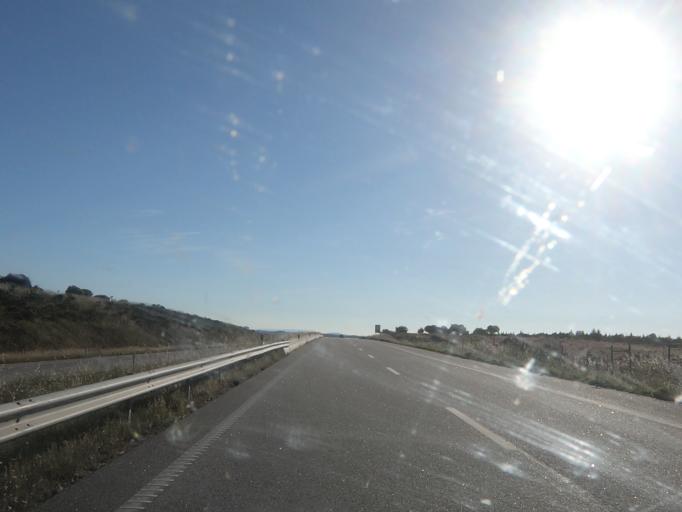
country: ES
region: Castille and Leon
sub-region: Provincia de Salamanca
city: Fuentes de Onoro
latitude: 40.6162
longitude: -6.8733
